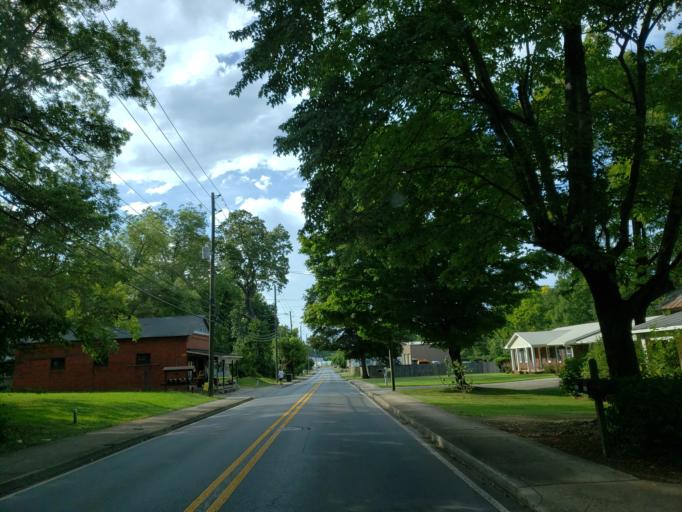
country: US
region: Georgia
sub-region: Bartow County
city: Cartersville
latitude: 34.1721
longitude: -84.8006
